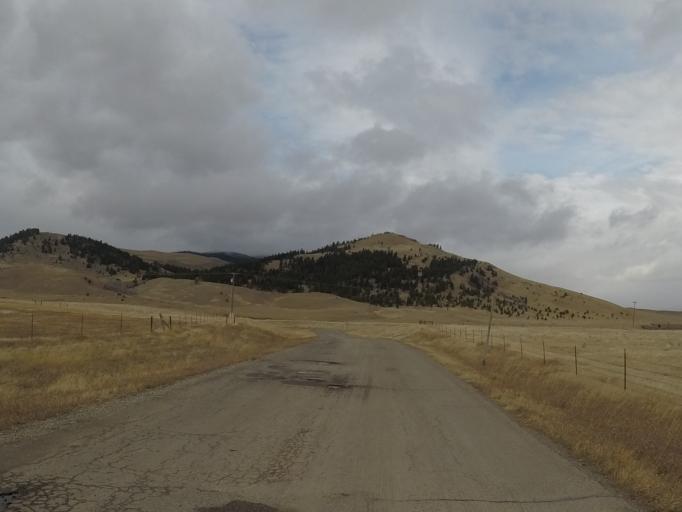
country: US
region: Montana
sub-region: Meagher County
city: White Sulphur Springs
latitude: 46.4265
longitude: -110.4175
